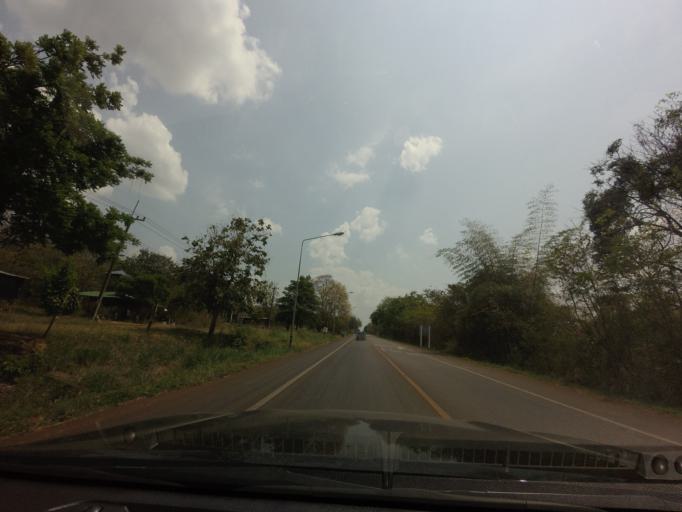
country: TH
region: Kanchanaburi
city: Sai Yok
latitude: 14.1340
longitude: 99.1562
